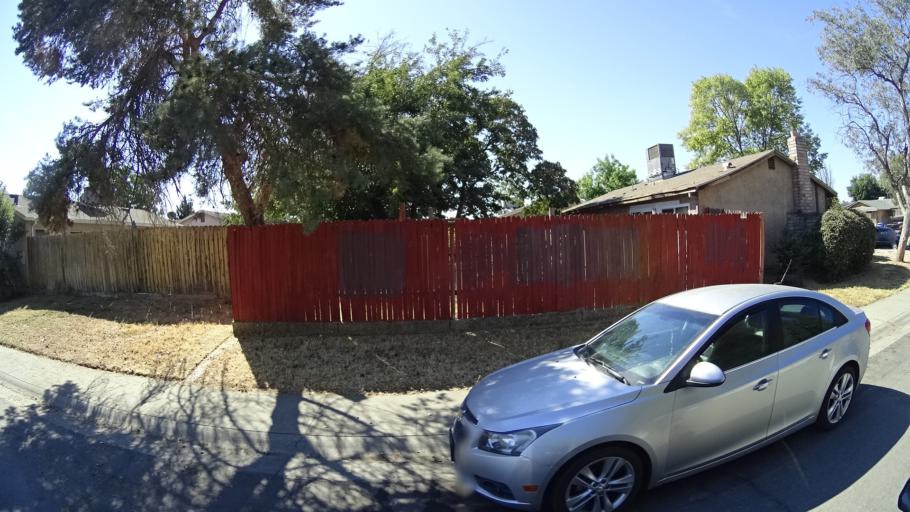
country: US
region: California
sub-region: Sacramento County
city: Parkway
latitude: 38.4655
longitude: -121.4419
